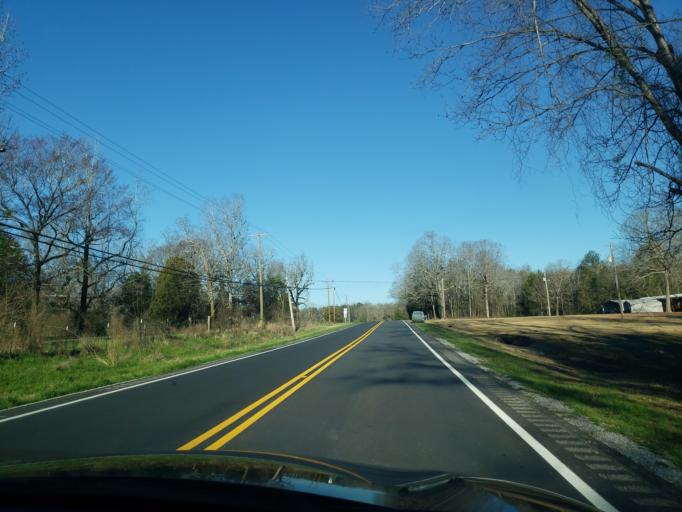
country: US
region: Alabama
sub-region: Macon County
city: Tuskegee
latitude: 32.5806
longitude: -85.7142
